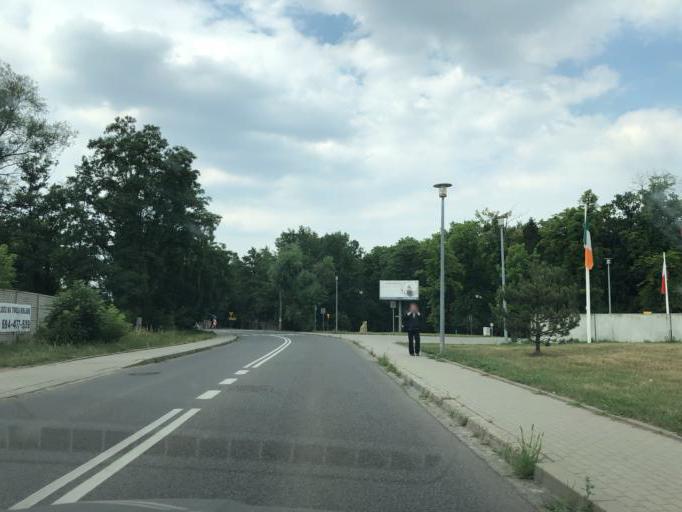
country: PL
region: Lesser Poland Voivodeship
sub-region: Powiat wielicki
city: Wieliczka
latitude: 49.9859
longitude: 20.0460
